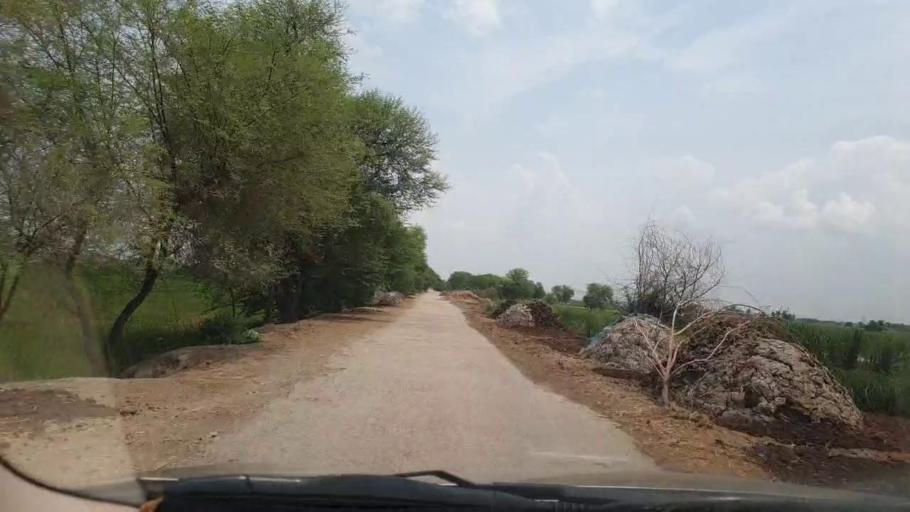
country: PK
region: Sindh
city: Larkana
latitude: 27.6084
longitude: 68.1508
